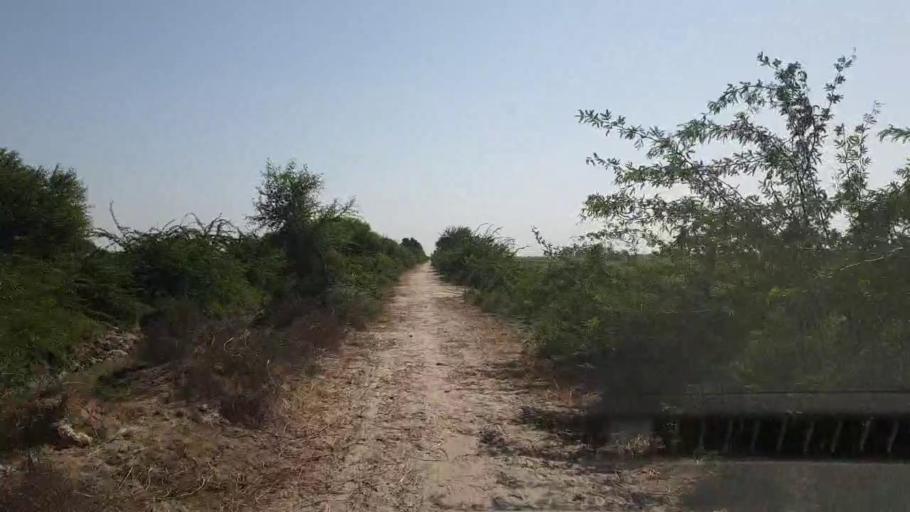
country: PK
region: Sindh
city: Kadhan
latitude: 24.6230
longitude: 68.9955
